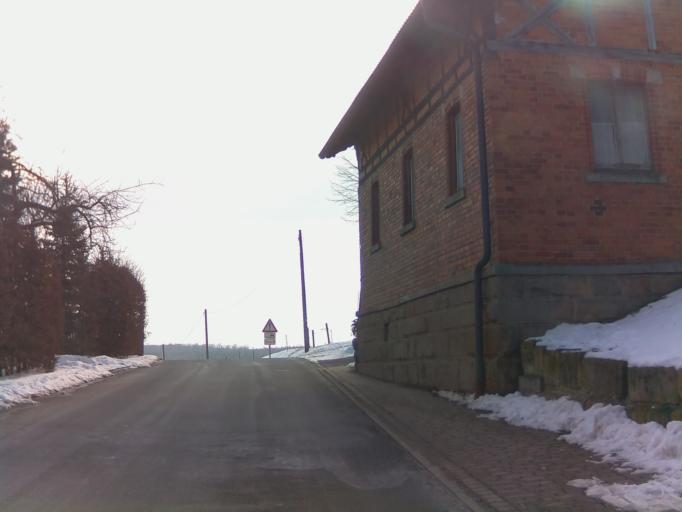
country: DE
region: Thuringia
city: Aschenhausen
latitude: 50.5745
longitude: 10.2092
